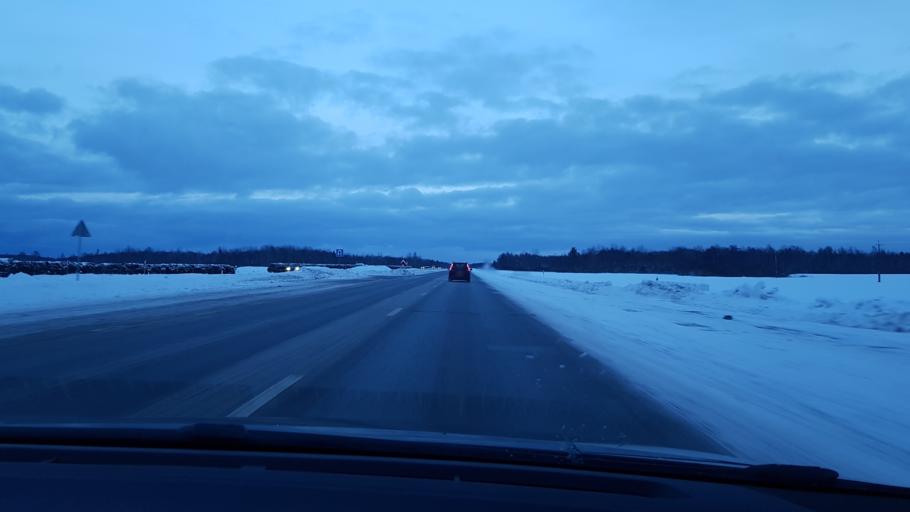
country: EE
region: Harju
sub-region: Anija vald
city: Kehra
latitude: 59.4414
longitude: 25.3096
